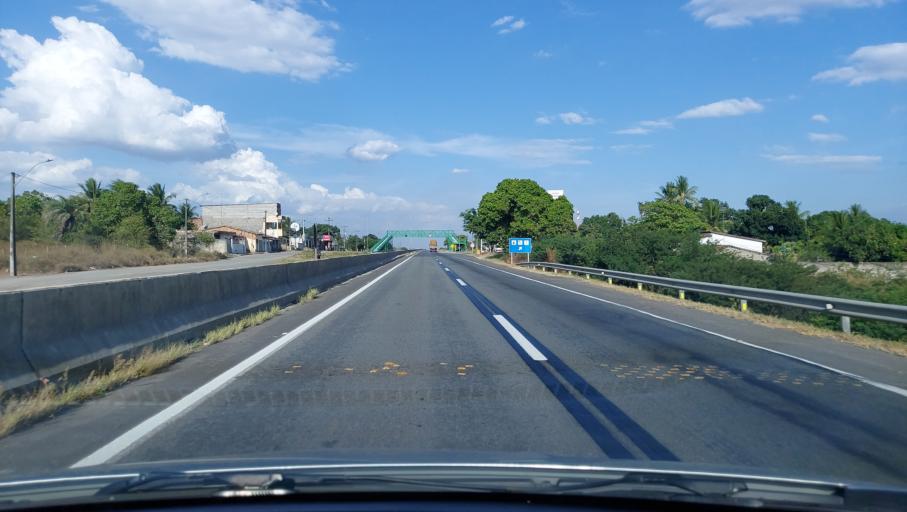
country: BR
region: Bahia
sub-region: Santo Estevao
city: Santo Estevao
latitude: -12.4622
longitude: -39.2742
